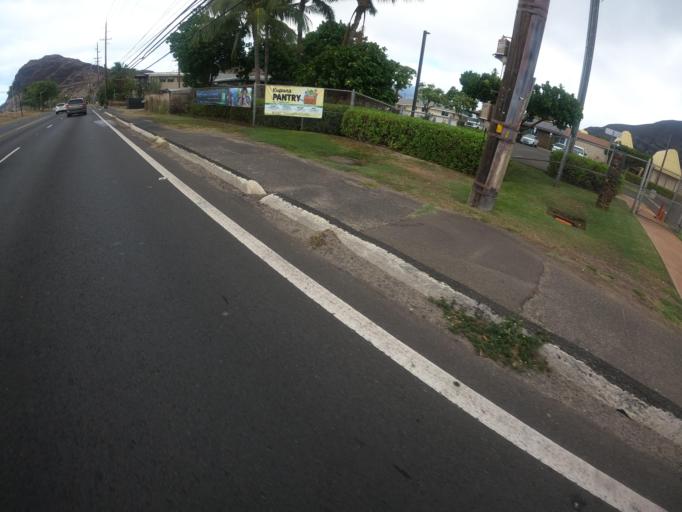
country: US
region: Hawaii
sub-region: Honolulu County
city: Nanakuli
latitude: 21.3905
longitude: -158.1552
